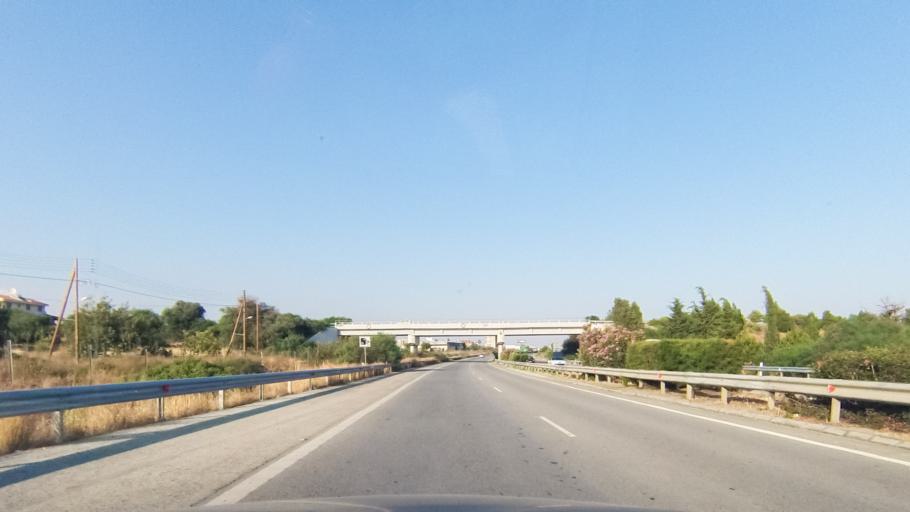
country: CY
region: Limassol
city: Ypsonas
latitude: 34.6963
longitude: 32.9520
